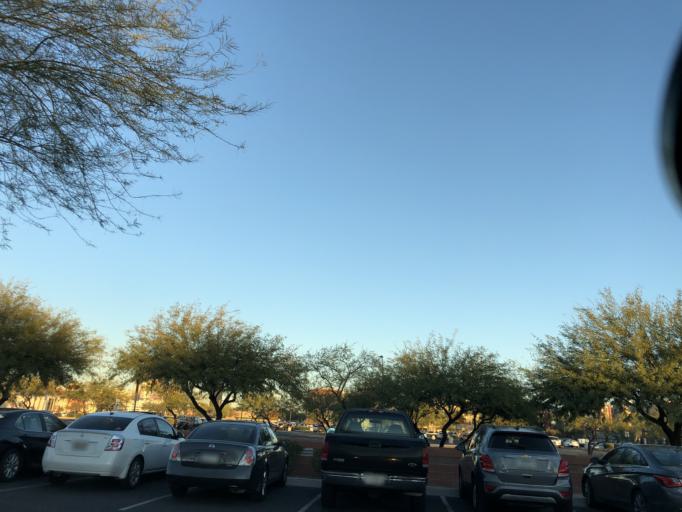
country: US
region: Arizona
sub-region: Maricopa County
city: Peoria
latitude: 33.5337
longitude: -112.2653
